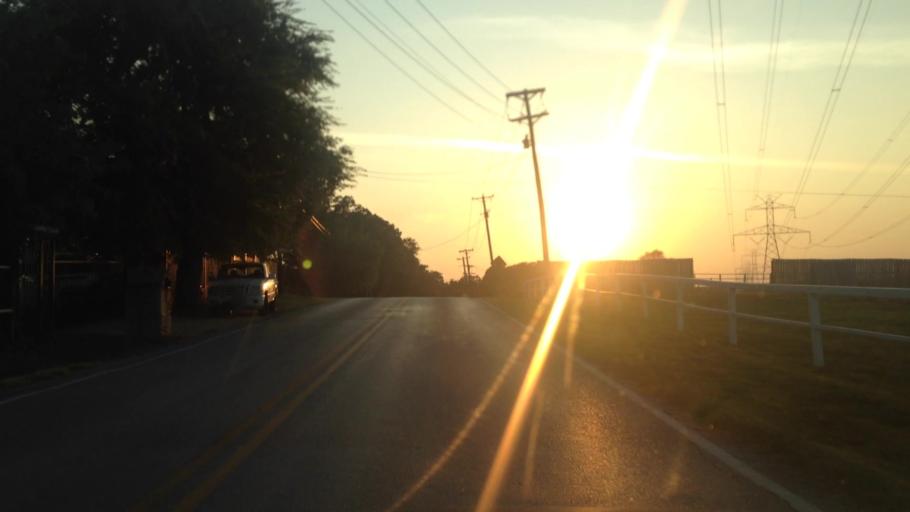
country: US
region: Texas
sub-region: Tarrant County
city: Kennedale
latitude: 32.6333
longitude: -97.2003
